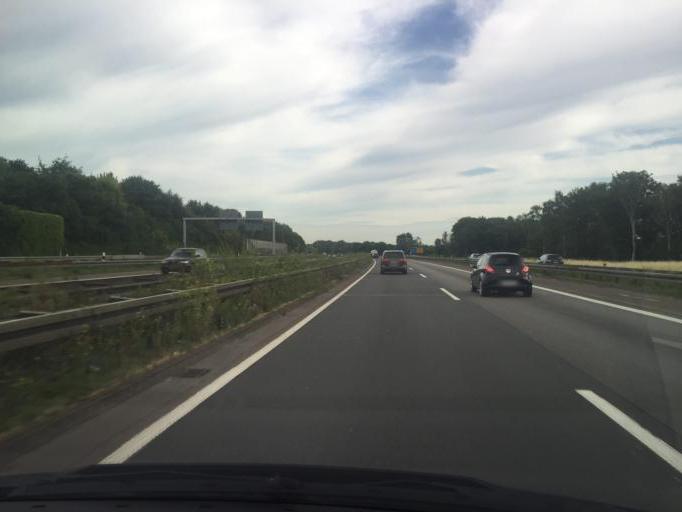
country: DE
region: North Rhine-Westphalia
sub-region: Regierungsbezirk Dusseldorf
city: Krefeld
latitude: 51.3685
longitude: 6.6259
